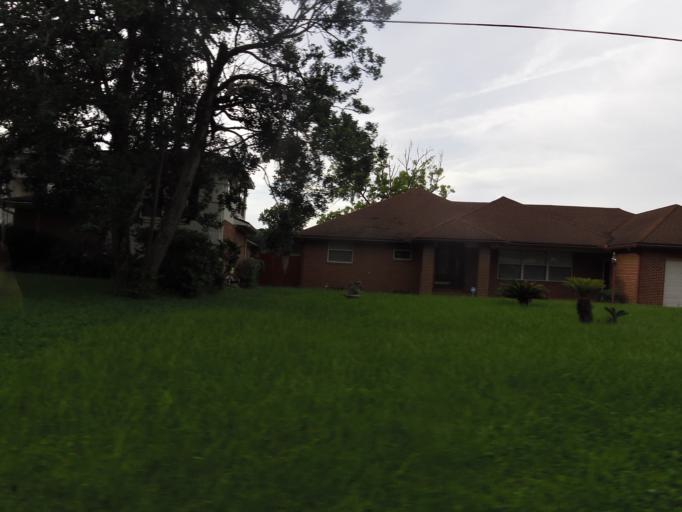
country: US
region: Florida
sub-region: Duval County
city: Jacksonville
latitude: 30.3986
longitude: -81.7025
